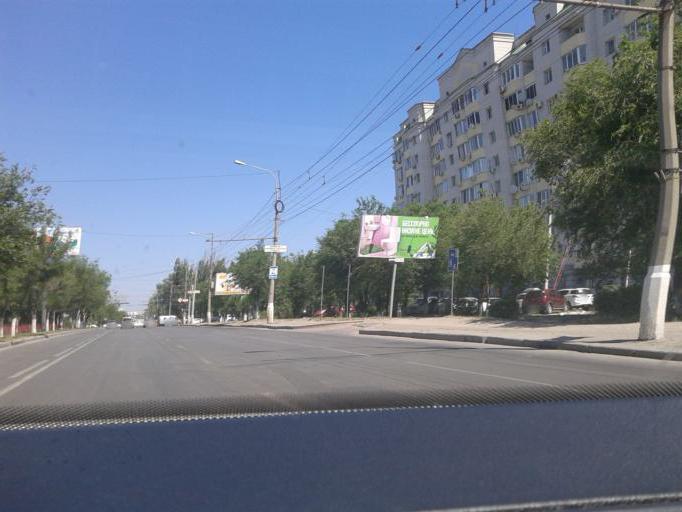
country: RU
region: Volgograd
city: Volgograd
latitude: 48.7333
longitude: 44.4960
